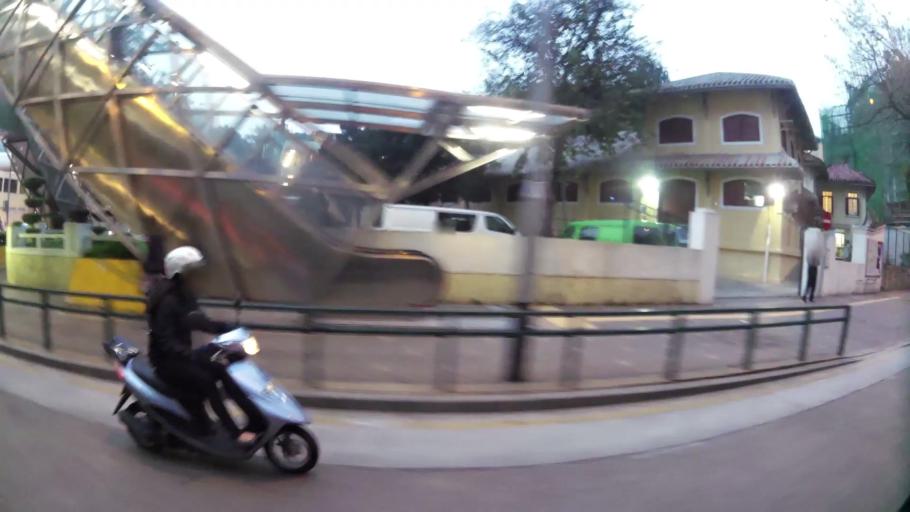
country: MO
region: Macau
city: Macau
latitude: 22.2074
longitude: 113.5461
